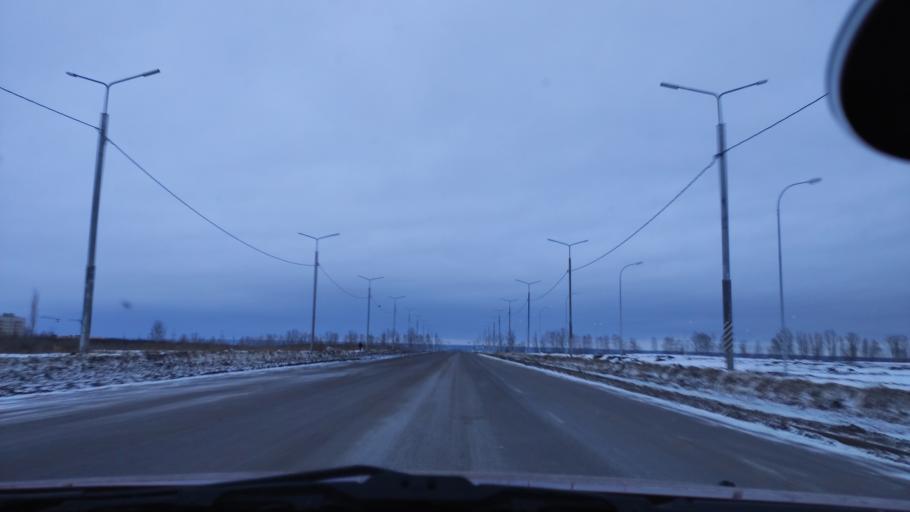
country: RU
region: Tambov
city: Tambov
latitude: 52.7784
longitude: 41.4155
